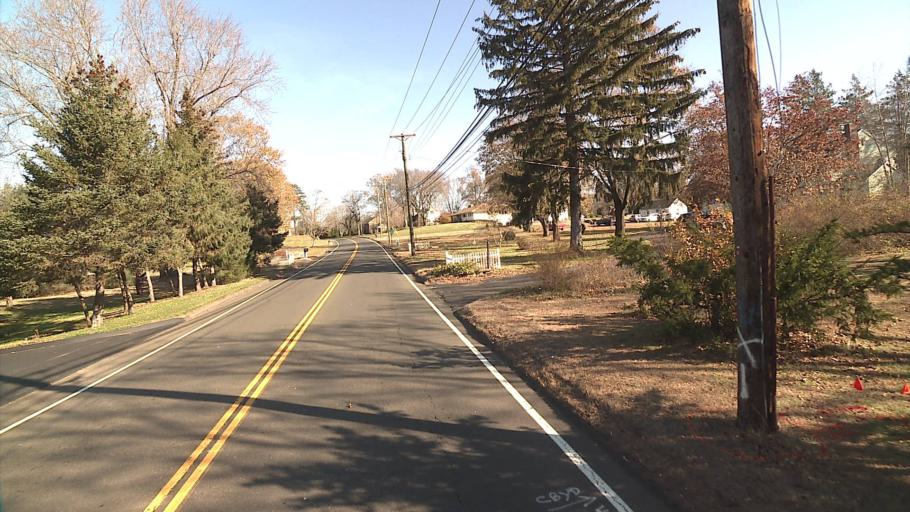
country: US
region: Connecticut
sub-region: New Haven County
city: North Haven
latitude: 41.3540
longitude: -72.8449
